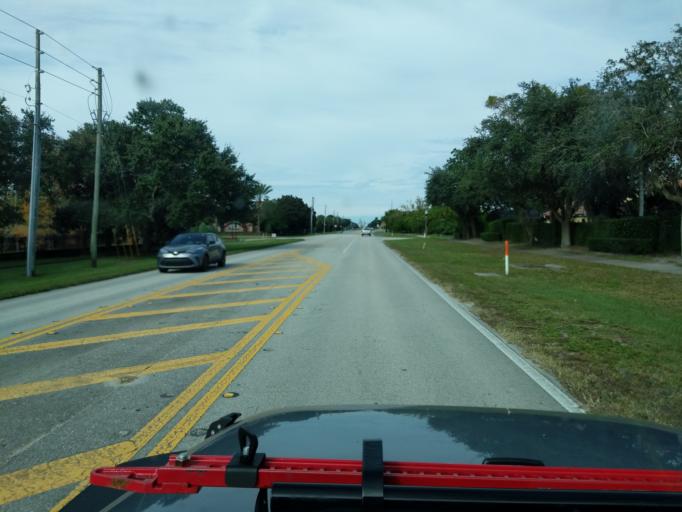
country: US
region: Florida
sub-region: Orange County
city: Gotha
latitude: 28.5246
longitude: -81.5417
